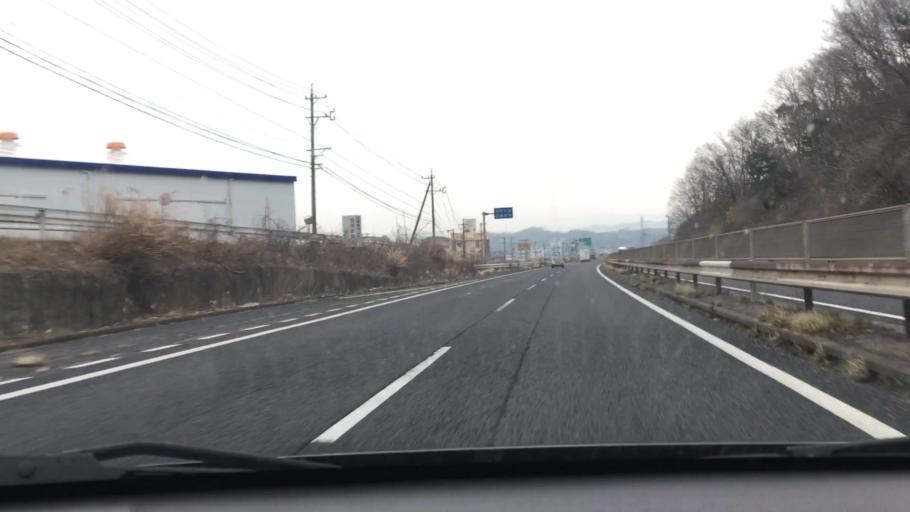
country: JP
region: Mie
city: Ueno-ebisumachi
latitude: 34.7363
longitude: 136.1052
